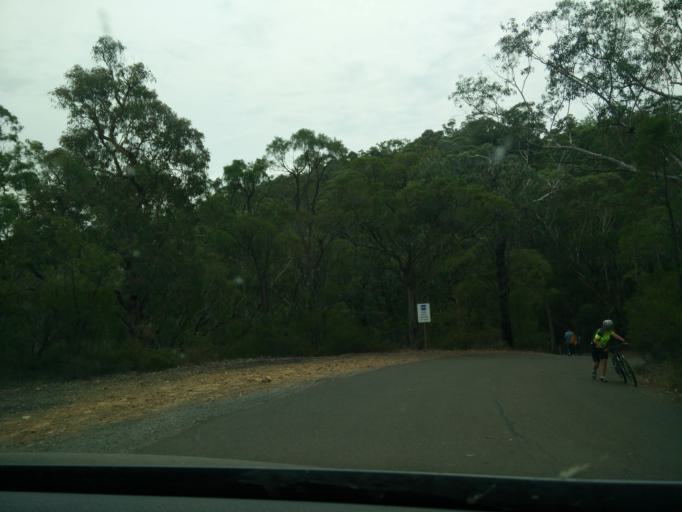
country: AU
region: New South Wales
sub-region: Blue Mountains Municipality
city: Glenbrook
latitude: -33.7772
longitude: 150.6194
